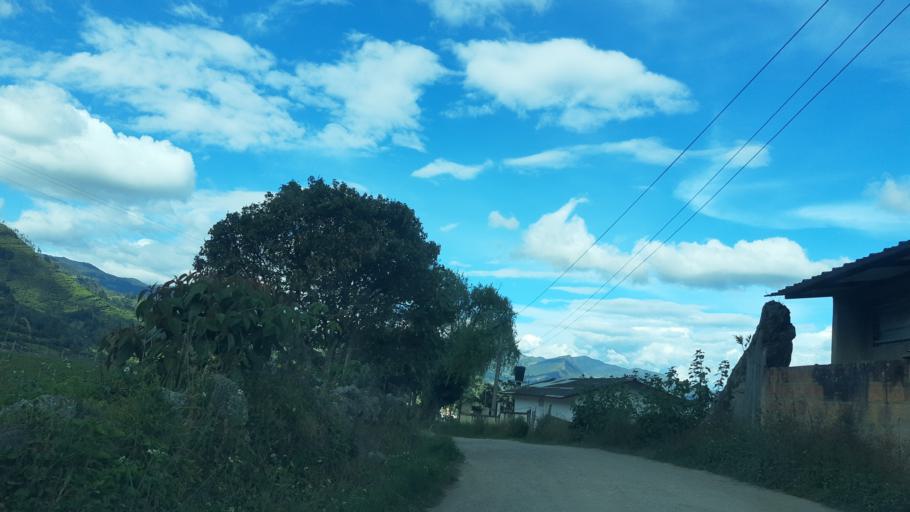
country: CO
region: Cundinamarca
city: Macheta
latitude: 5.0714
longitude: -73.6237
